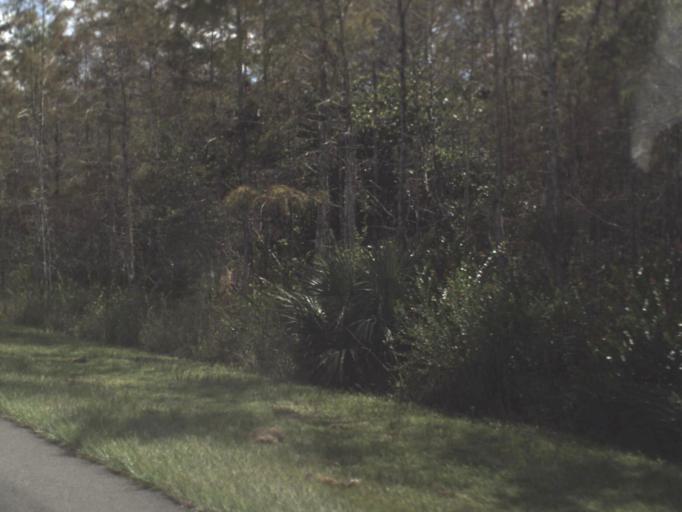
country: US
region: Florida
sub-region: Miami-Dade County
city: Kendall West
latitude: 25.8392
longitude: -80.9125
